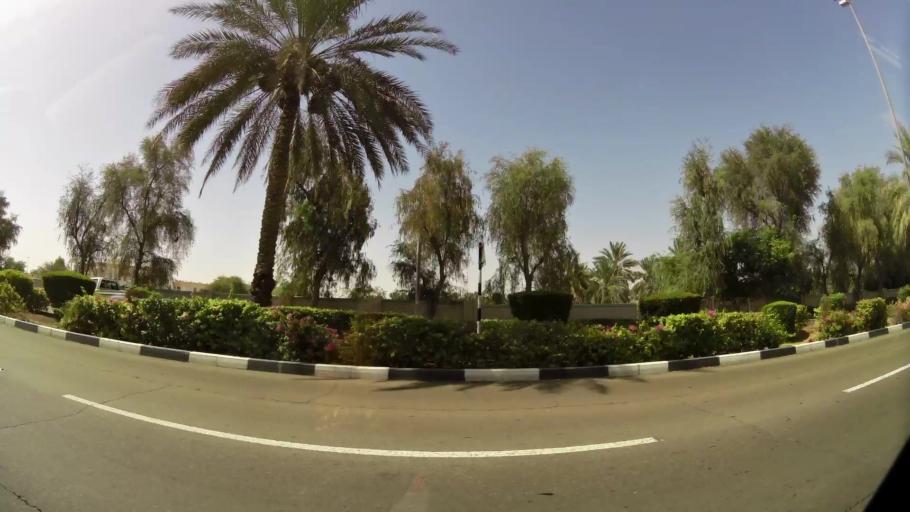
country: OM
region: Al Buraimi
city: Al Buraymi
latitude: 24.2976
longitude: 55.7812
